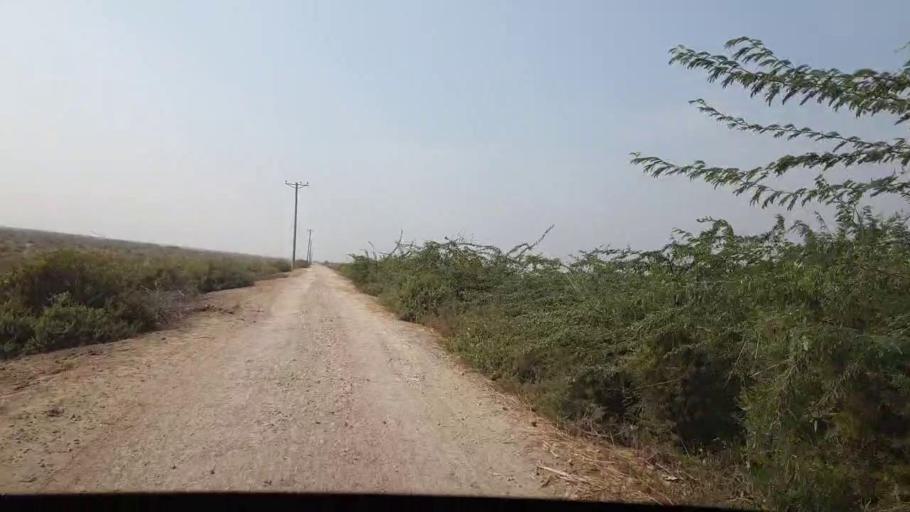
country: PK
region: Sindh
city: Chuhar Jamali
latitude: 24.2703
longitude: 67.8927
